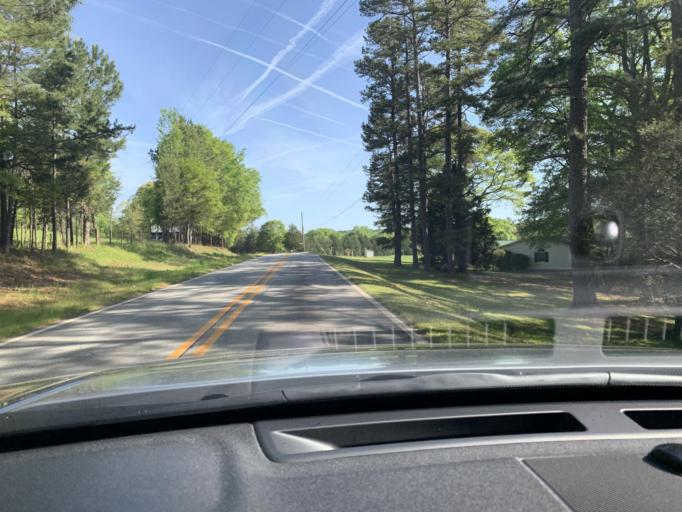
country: US
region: Georgia
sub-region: Oconee County
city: Watkinsville
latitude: 33.8074
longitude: -83.3144
